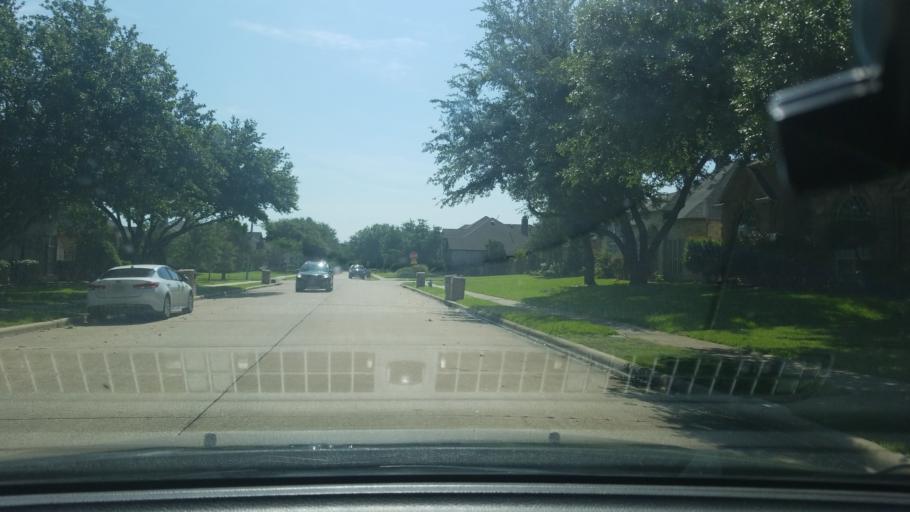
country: US
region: Texas
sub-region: Dallas County
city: Mesquite
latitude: 32.7749
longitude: -96.5837
